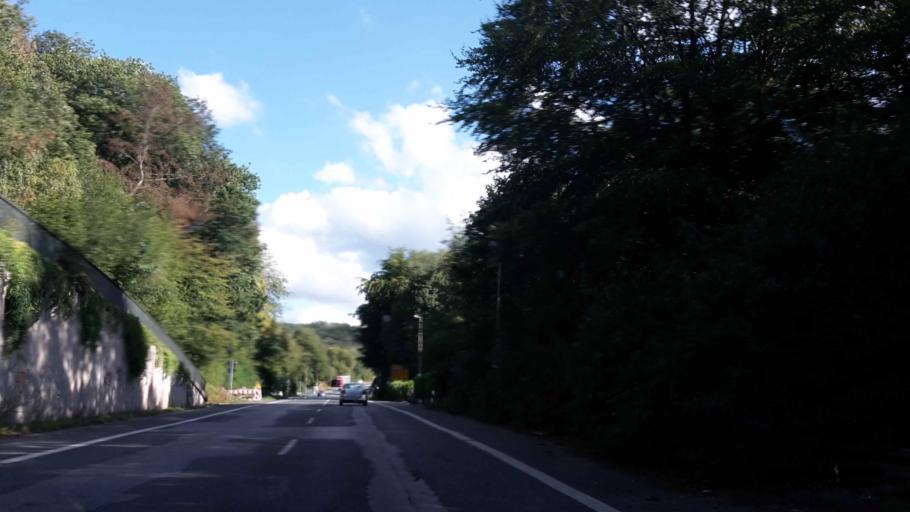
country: DE
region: North Rhine-Westphalia
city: Sprockhovel
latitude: 51.3648
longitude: 7.2549
